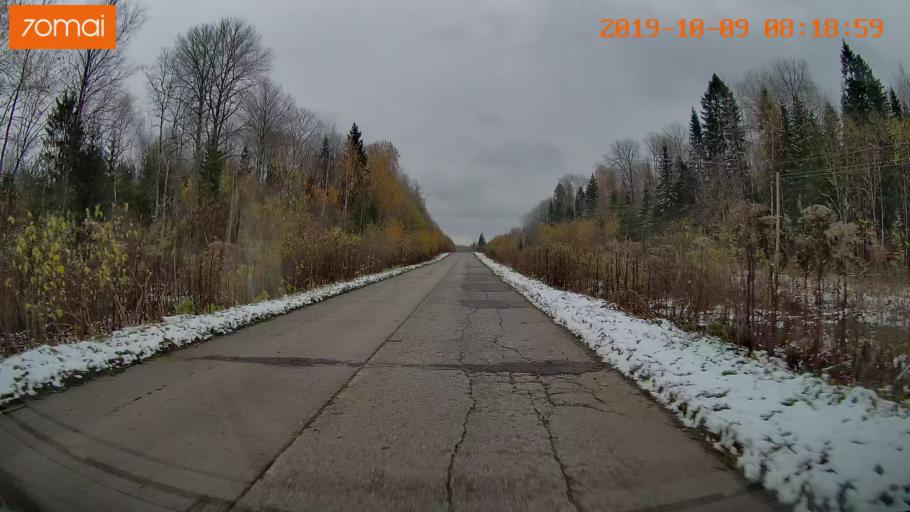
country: RU
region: Vologda
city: Gryazovets
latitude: 58.7413
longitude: 40.2337
